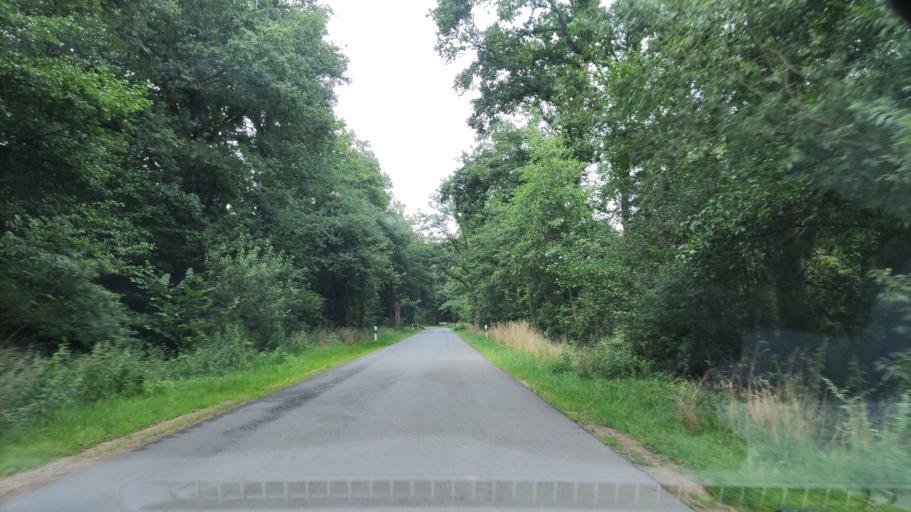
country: DE
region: Lower Saxony
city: Dannenberg
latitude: 53.0919
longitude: 11.1283
